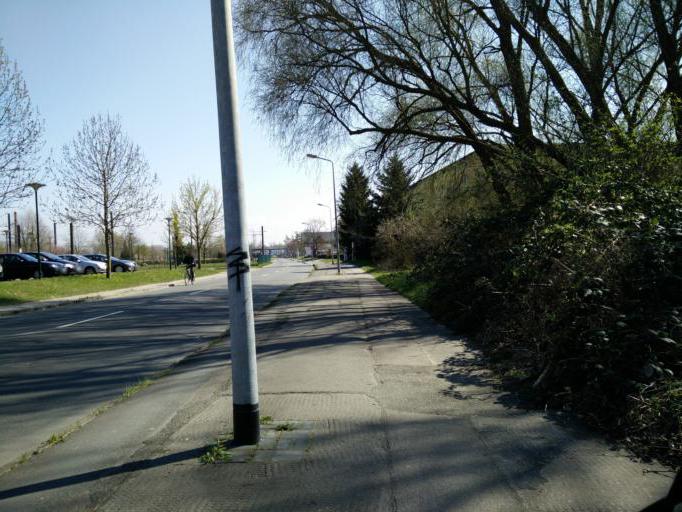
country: DE
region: Mecklenburg-Vorpommern
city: Lambrechtshagen
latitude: 54.1123
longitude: 12.0781
